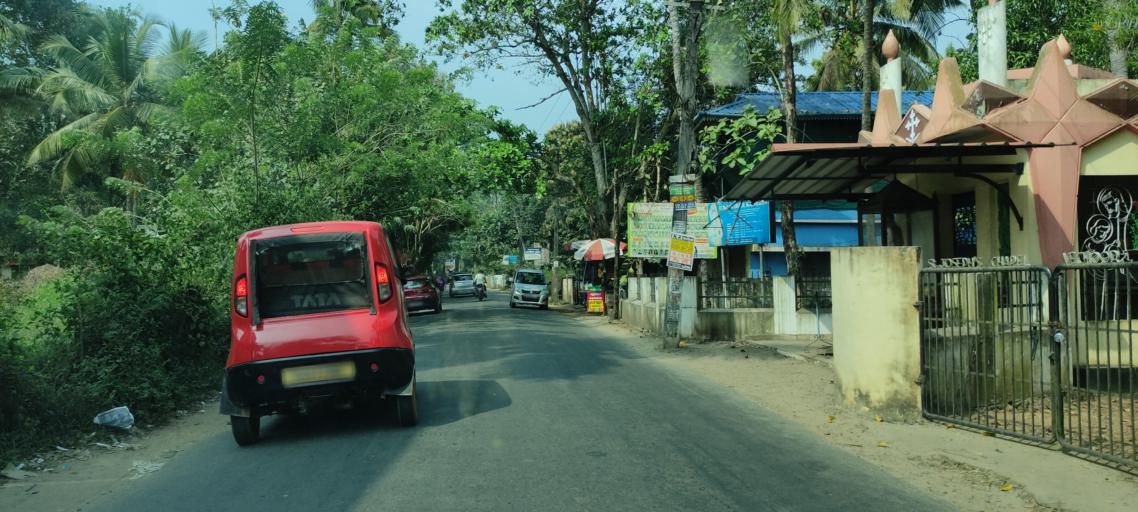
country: IN
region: Kerala
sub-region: Alappuzha
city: Shertallai
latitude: 9.6743
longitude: 76.4215
